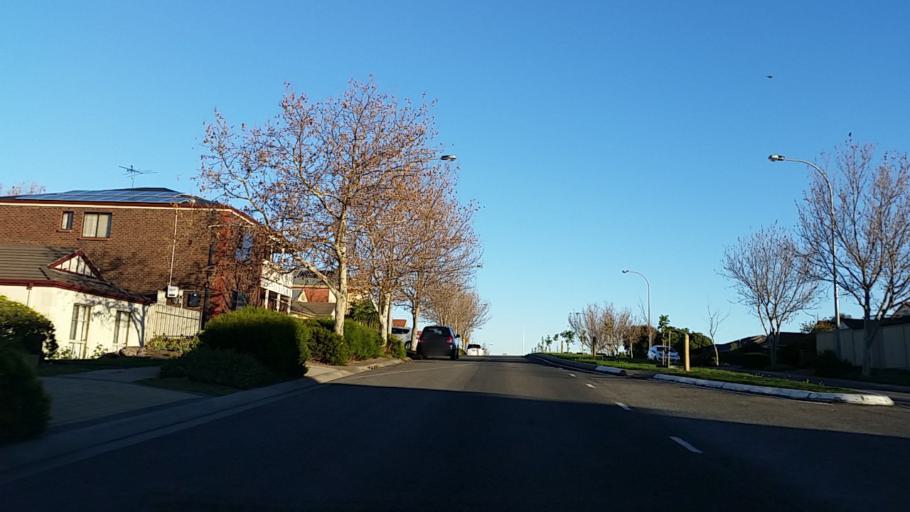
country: AU
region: South Australia
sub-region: Onkaparinga
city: Moana
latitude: -35.2026
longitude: 138.4877
